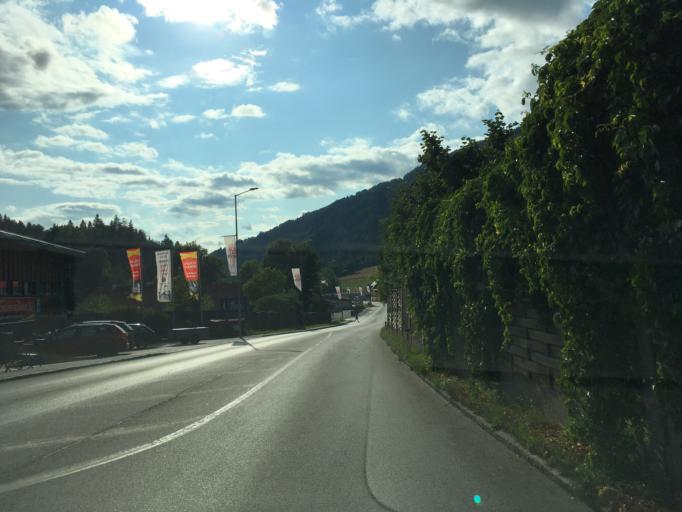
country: AT
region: Styria
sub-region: Politischer Bezirk Murau
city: Murau
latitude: 47.1127
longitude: 14.1660
